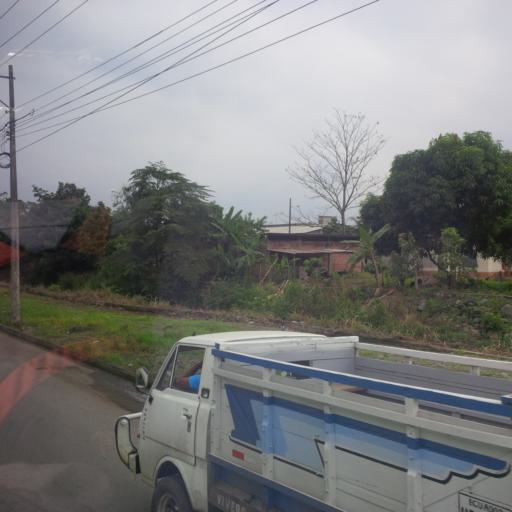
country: EC
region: Canar
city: La Troncal
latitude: -2.3352
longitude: -79.3996
